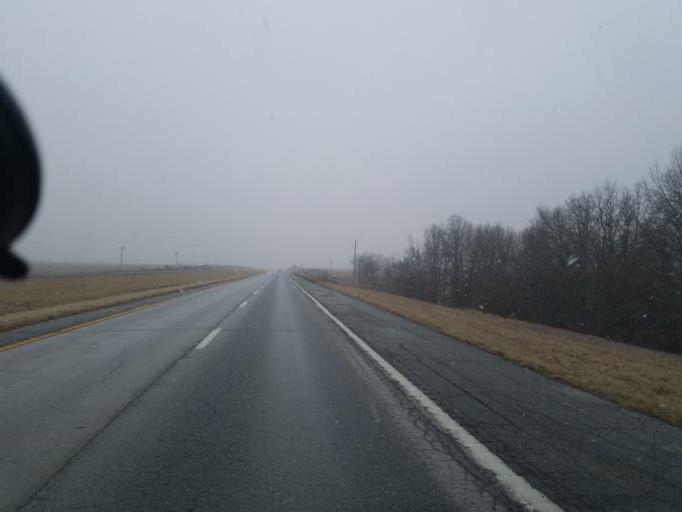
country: US
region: Missouri
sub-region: Macon County
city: La Plata
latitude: 39.9637
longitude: -92.4766
